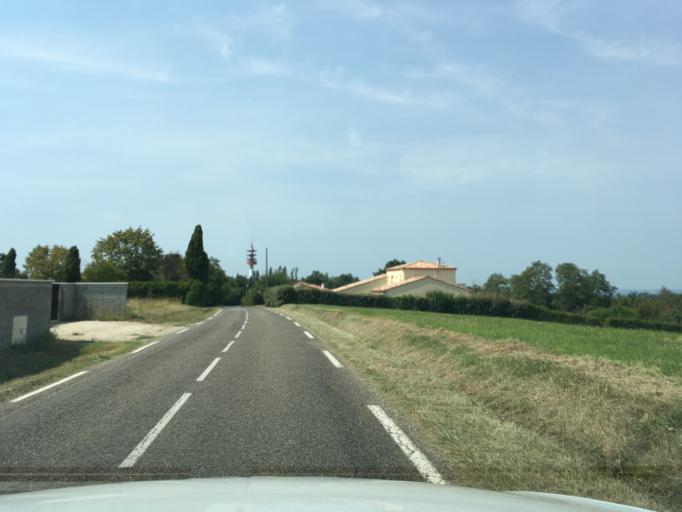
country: FR
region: Midi-Pyrenees
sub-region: Departement du Tarn-et-Garonne
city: Corbarieu
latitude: 43.9641
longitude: 1.3853
